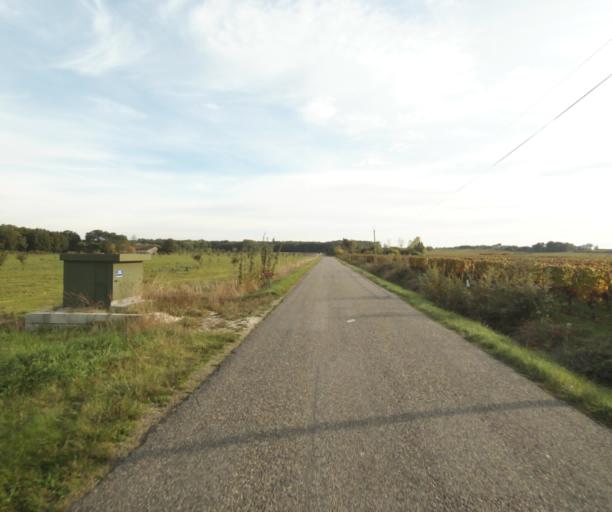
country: FR
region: Midi-Pyrenees
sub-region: Departement du Tarn-et-Garonne
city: Campsas
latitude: 43.8785
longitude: 1.3393
